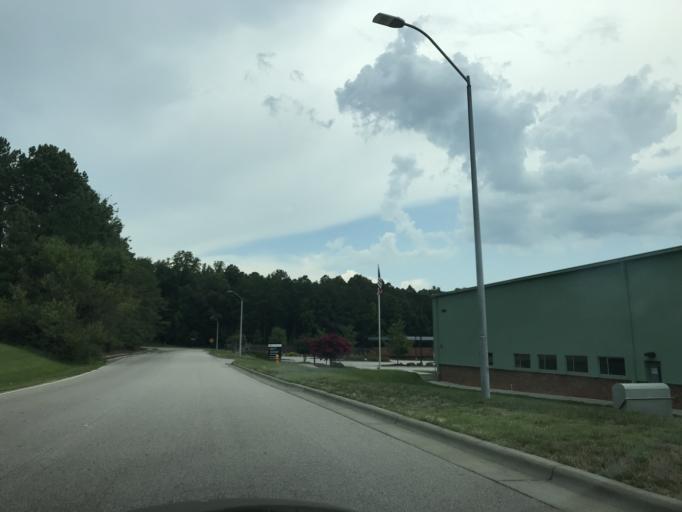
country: US
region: North Carolina
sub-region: Wake County
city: Wake Forest
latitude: 35.8876
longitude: -78.5768
